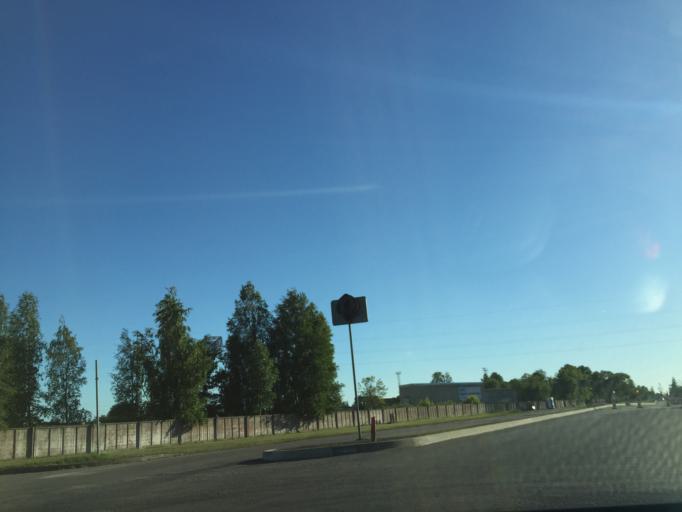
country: LV
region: Ventspils
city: Ventspils
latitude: 57.3974
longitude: 21.6271
